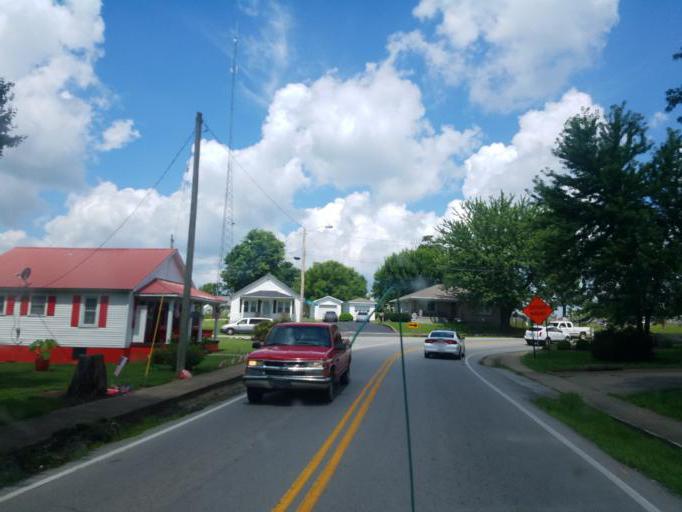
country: US
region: Kentucky
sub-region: Grayson County
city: Leitchfield
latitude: 37.4886
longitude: -86.2935
